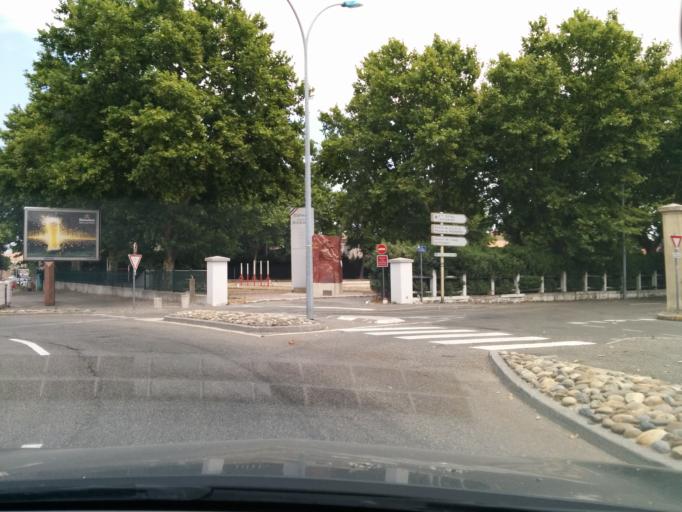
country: FR
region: Languedoc-Roussillon
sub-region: Departement de l'Aude
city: Carcassonne
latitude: 43.2102
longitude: 2.3524
